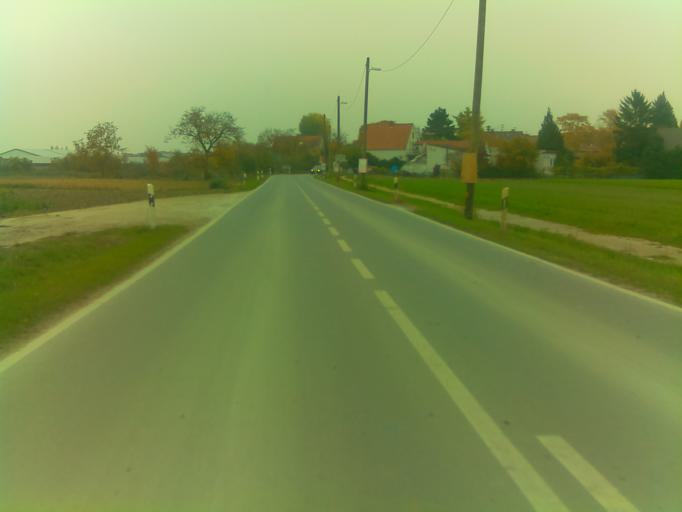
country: DE
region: Rheinland-Pfalz
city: Fussgonheim
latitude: 49.4697
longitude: 8.3162
